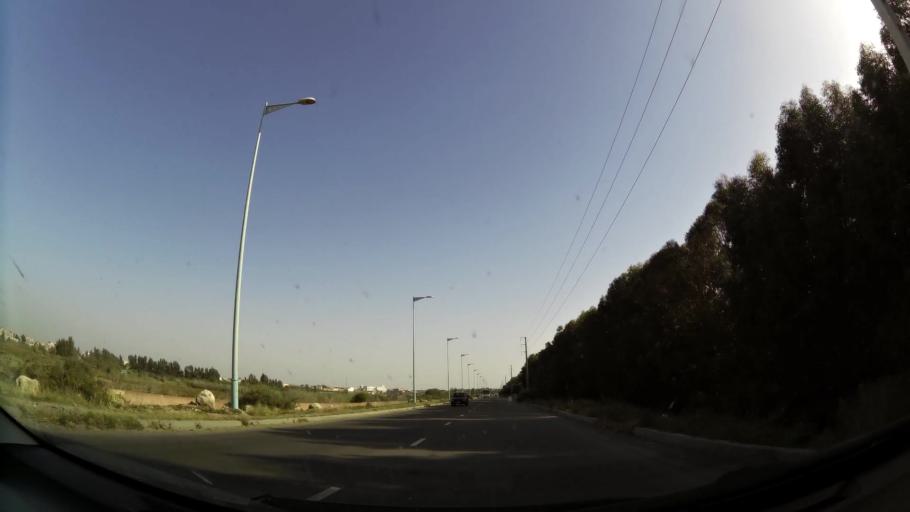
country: MA
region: Souss-Massa-Draa
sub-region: Inezgane-Ait Mellou
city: Inezgane
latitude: 30.3577
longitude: -9.5059
